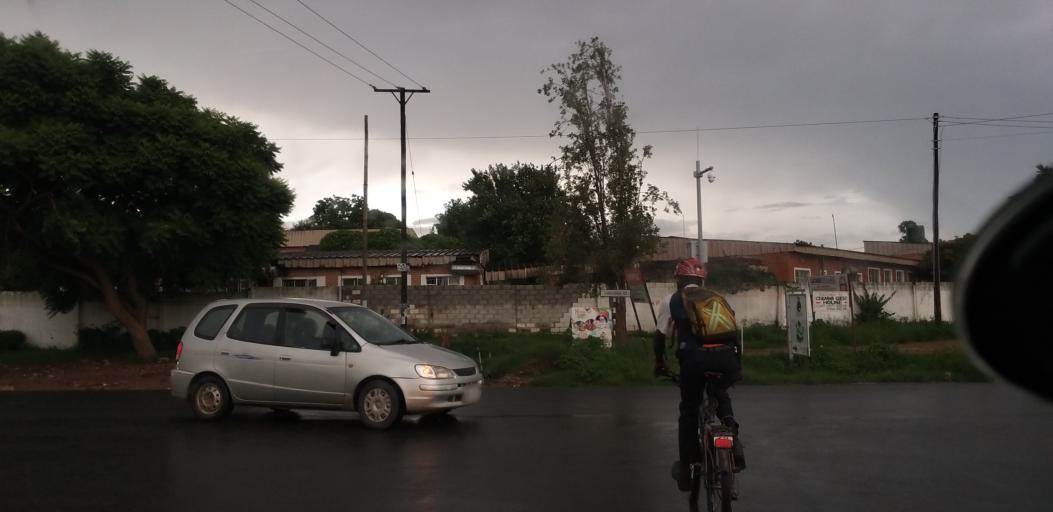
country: ZM
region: Lusaka
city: Lusaka
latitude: -15.4209
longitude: 28.3573
